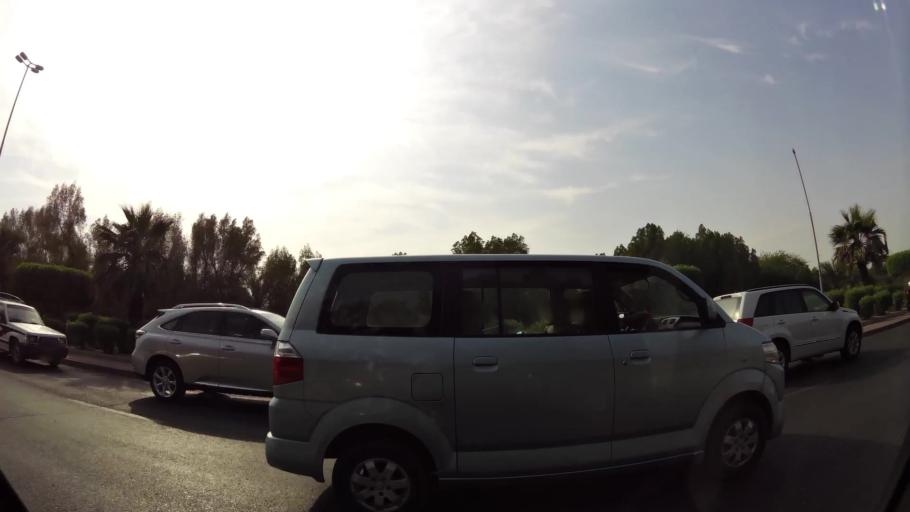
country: KW
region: Al Farwaniyah
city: Al Farwaniyah
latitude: 29.2986
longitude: 47.9645
